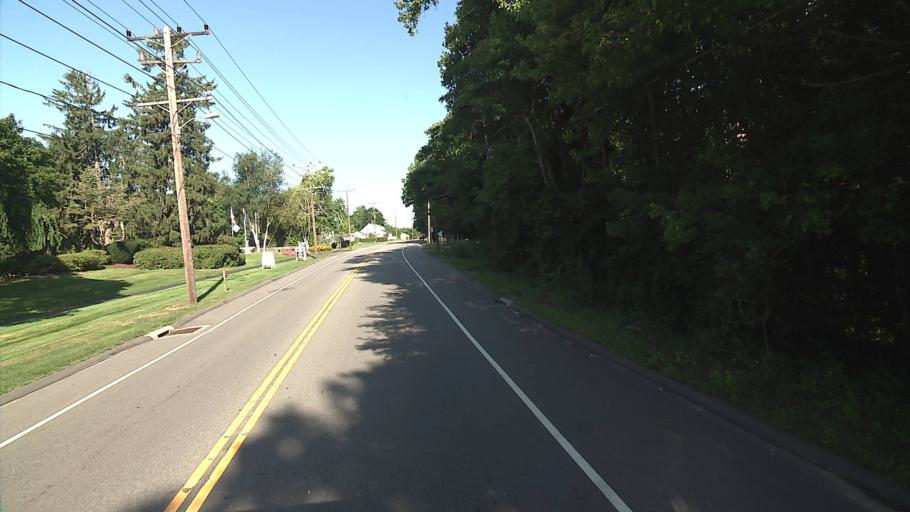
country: US
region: Connecticut
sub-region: Middlesex County
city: Westbrook Center
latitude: 41.2815
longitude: -72.4372
